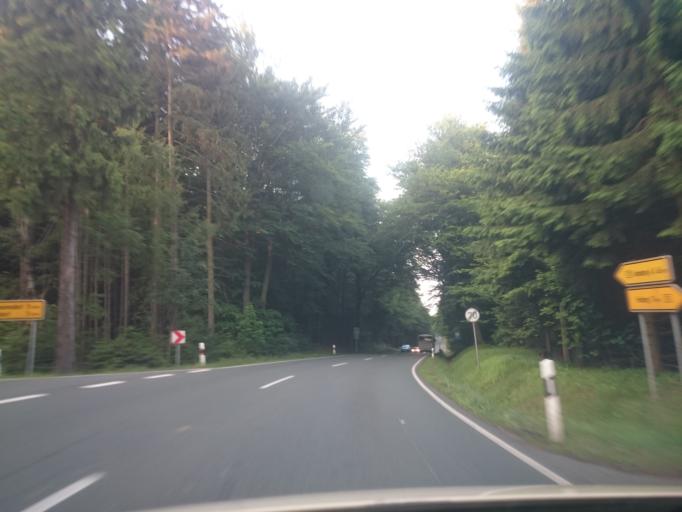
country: DE
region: Saxony
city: Grosshartmannsdorf
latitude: 50.8234
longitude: 13.3270
